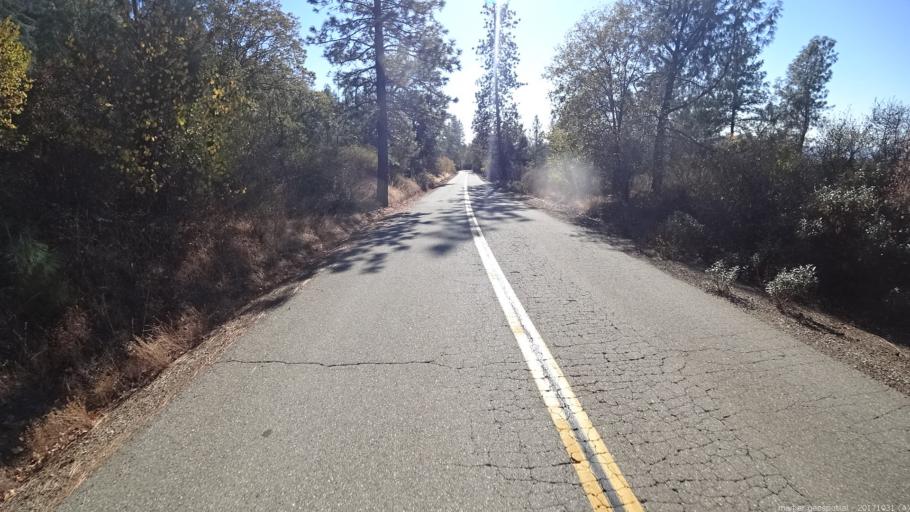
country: US
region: California
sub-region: Shasta County
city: Shingletown
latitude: 40.4606
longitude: -122.0034
